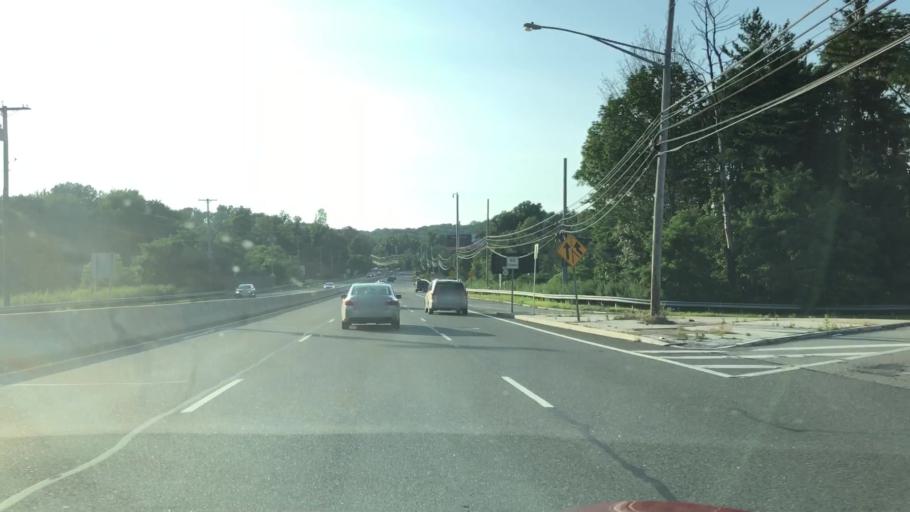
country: US
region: New Jersey
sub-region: Morris County
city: Morris Plains
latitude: 40.8508
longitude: -74.4731
